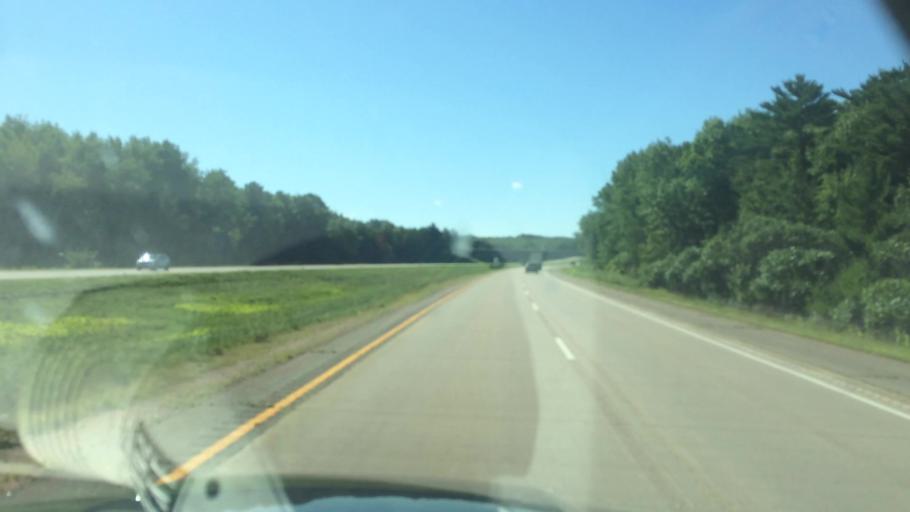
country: US
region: Wisconsin
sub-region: Marathon County
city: Mosinee
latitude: 44.7174
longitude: -89.6639
